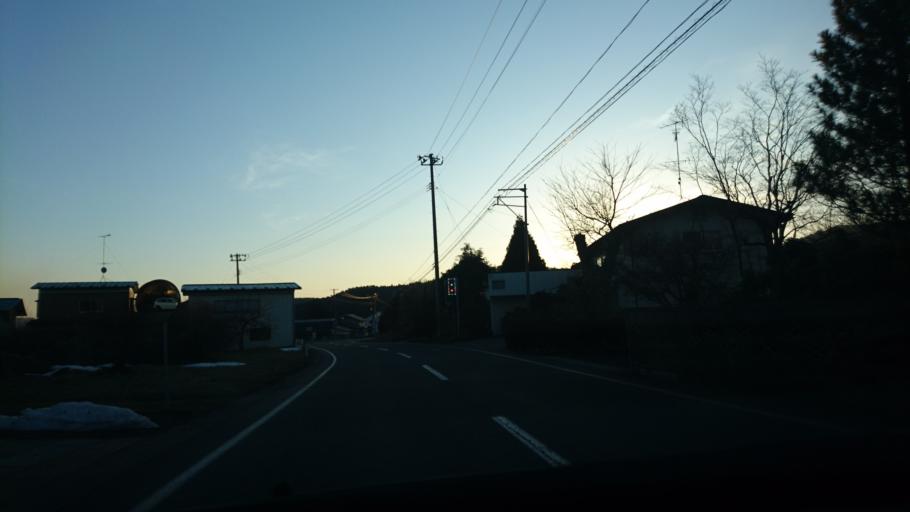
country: JP
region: Iwate
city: Mizusawa
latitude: 39.0355
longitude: 141.2974
